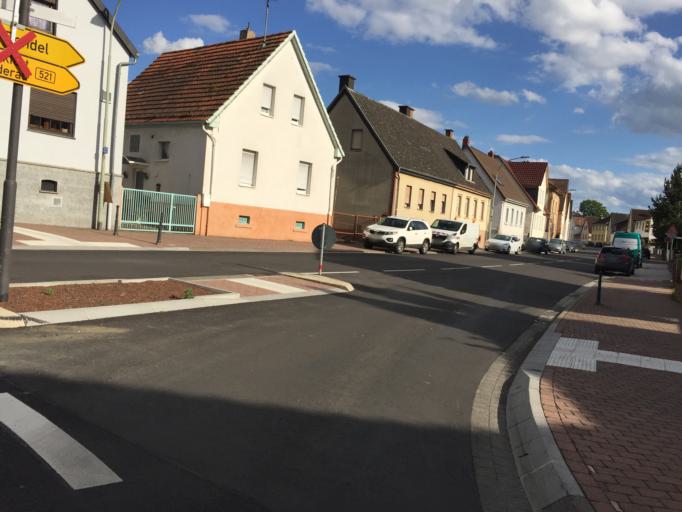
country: DE
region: Hesse
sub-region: Regierungsbezirk Darmstadt
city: Karben
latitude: 50.2301
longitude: 8.7729
